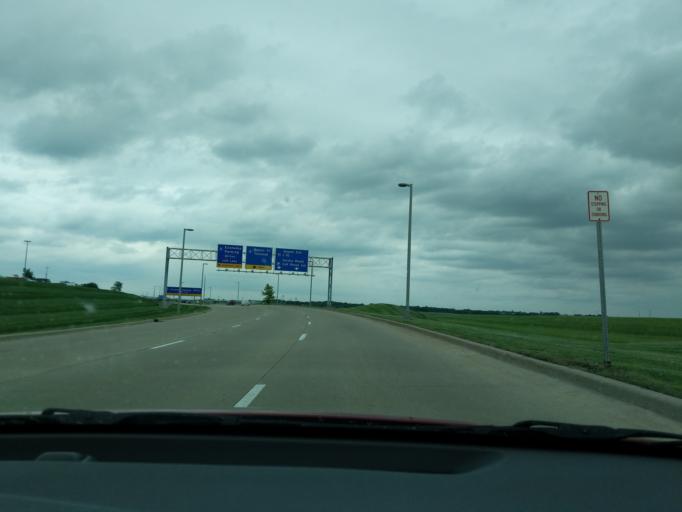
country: US
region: Indiana
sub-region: Hendricks County
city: Plainfield
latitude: 39.7084
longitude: -86.3103
